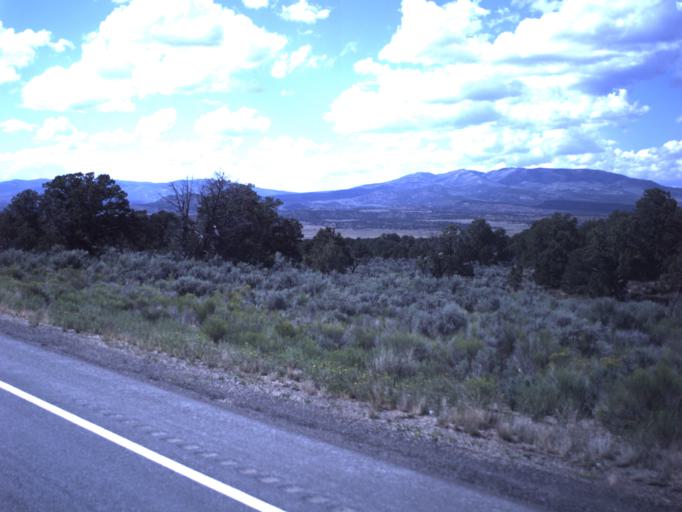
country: US
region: Utah
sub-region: Duchesne County
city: Duchesne
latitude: 40.2007
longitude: -110.7022
